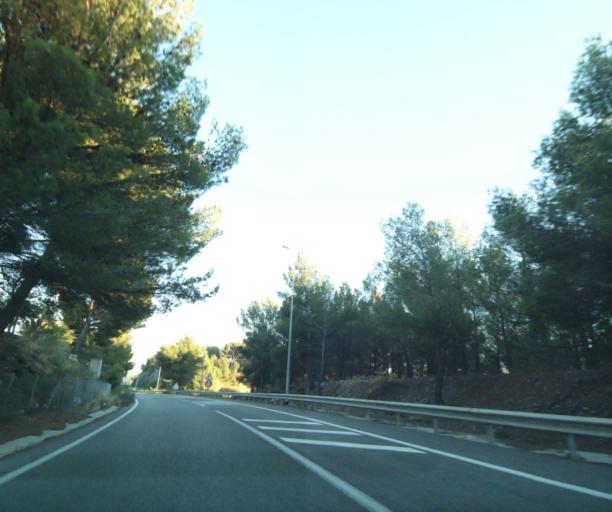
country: FR
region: Provence-Alpes-Cote d'Azur
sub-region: Departement des Bouches-du-Rhone
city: La Ciotat
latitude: 43.2043
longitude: 5.5904
